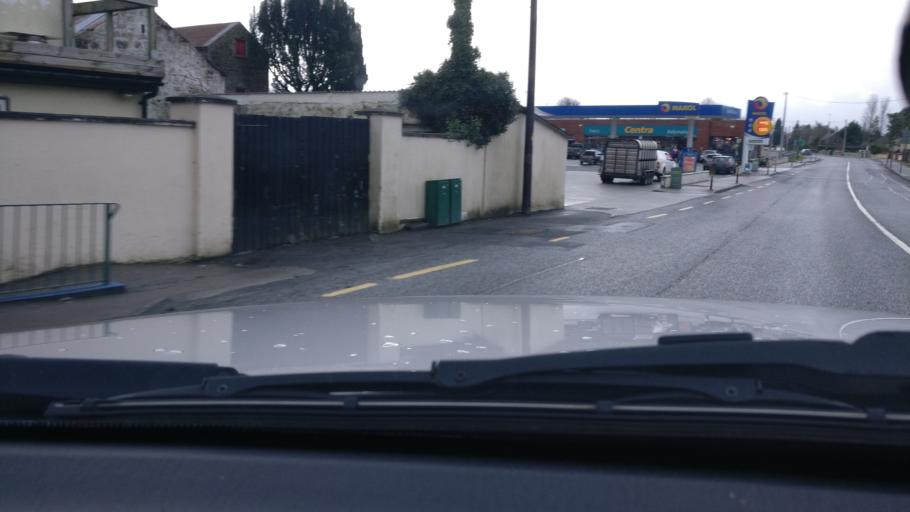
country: IE
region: Leinster
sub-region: An Longfort
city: Ballymahon
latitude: 53.5615
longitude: -7.7617
